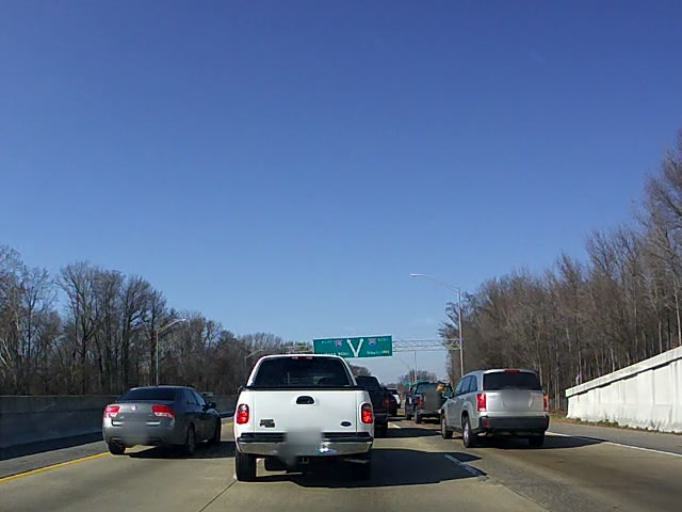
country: US
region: Tennessee
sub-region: Shelby County
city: Germantown
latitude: 35.0793
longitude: -89.8727
